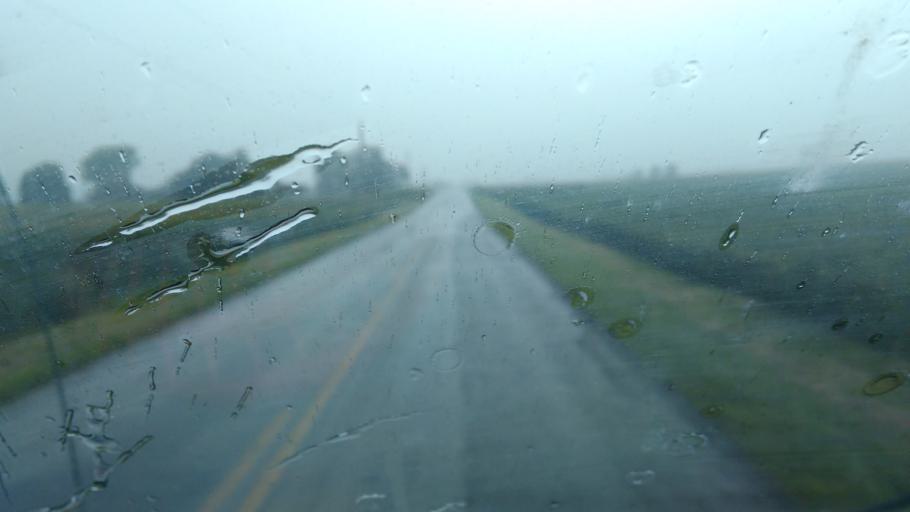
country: US
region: Ohio
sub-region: Hardin County
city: Kenton
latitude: 40.6888
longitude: -83.5379
